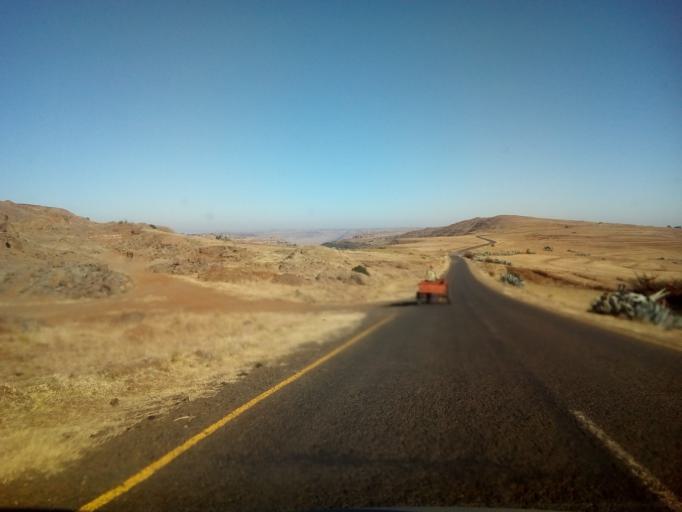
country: LS
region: Berea
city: Teyateyaneng
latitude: -29.2536
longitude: 27.7848
